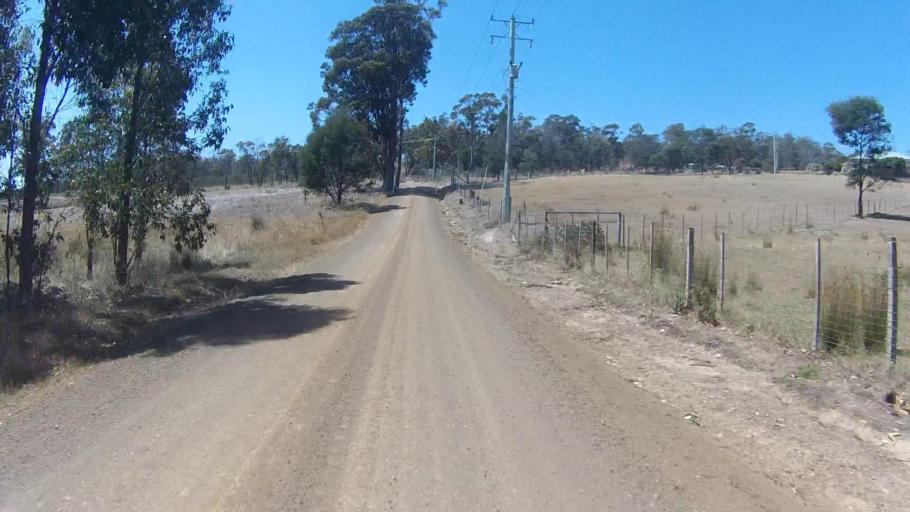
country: AU
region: Tasmania
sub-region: Sorell
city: Sorell
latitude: -42.8286
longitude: 147.6550
